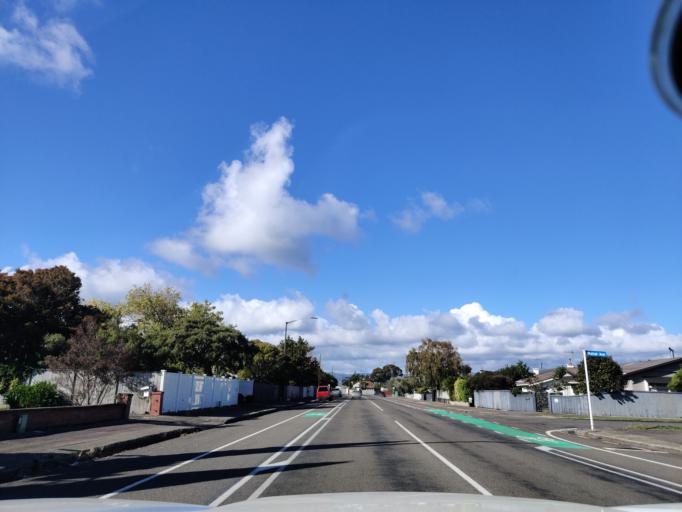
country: NZ
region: Manawatu-Wanganui
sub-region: Palmerston North City
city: Palmerston North
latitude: -40.3513
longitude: 175.5984
